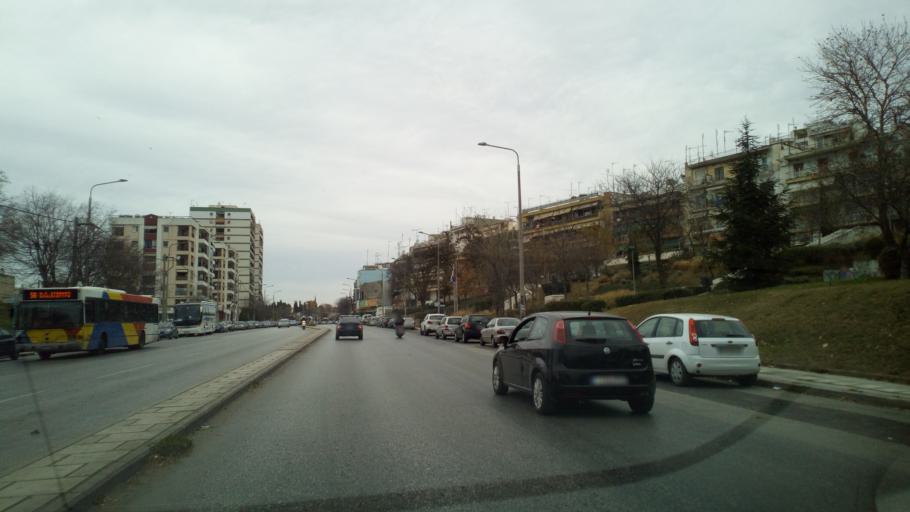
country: GR
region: Central Macedonia
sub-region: Nomos Thessalonikis
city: Thessaloniki
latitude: 40.6449
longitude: 22.9352
